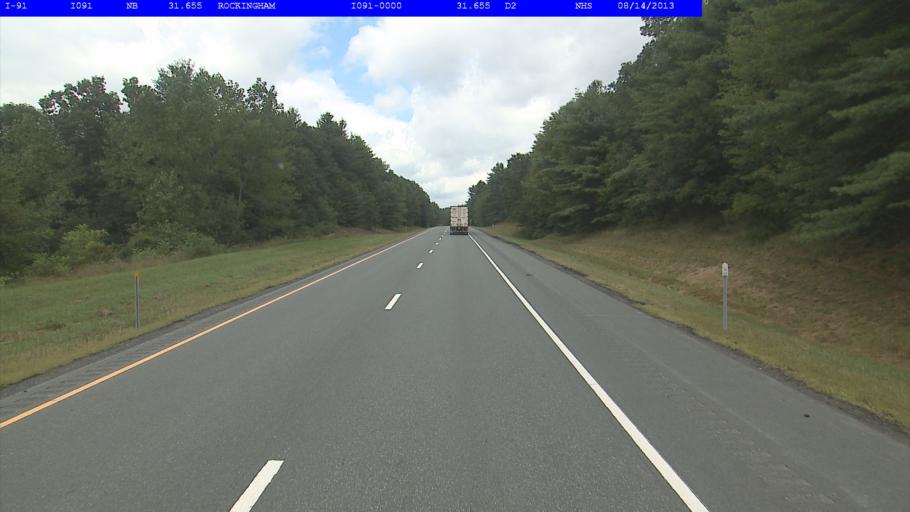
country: US
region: Vermont
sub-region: Windham County
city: Bellows Falls
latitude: 43.1307
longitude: -72.4736
